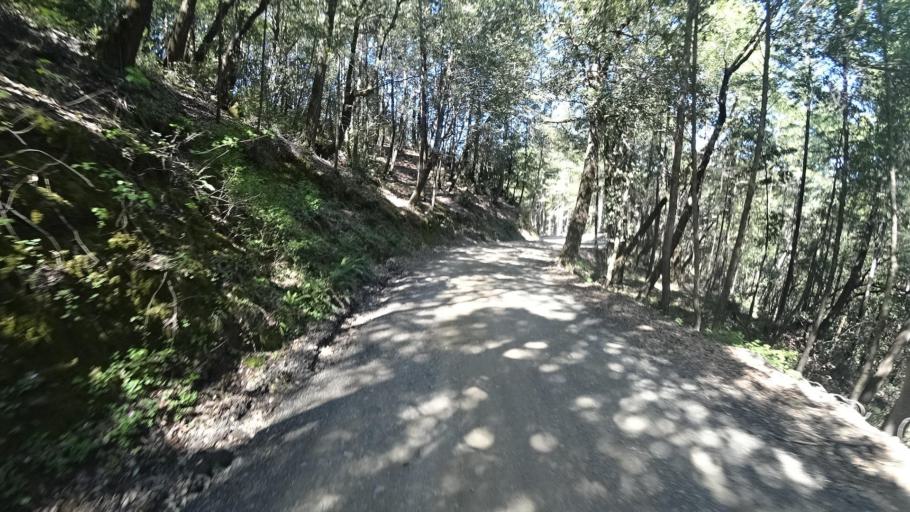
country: US
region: California
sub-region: Humboldt County
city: Rio Dell
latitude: 40.2173
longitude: -124.1083
